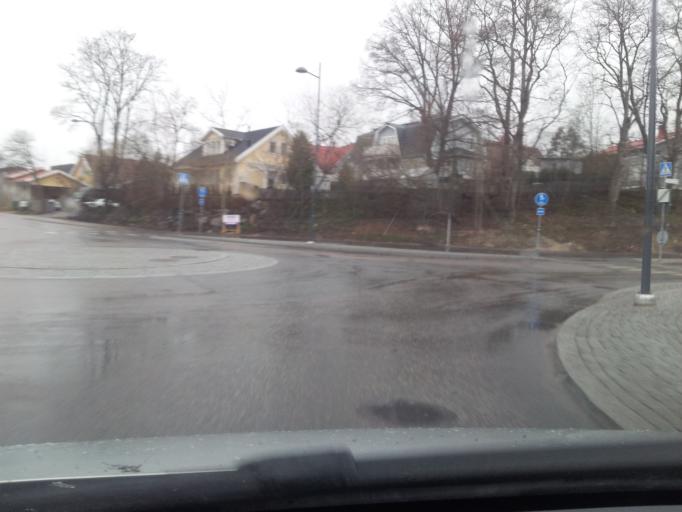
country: FI
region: Uusimaa
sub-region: Helsinki
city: Espoo
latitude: 60.1938
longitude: 24.6005
